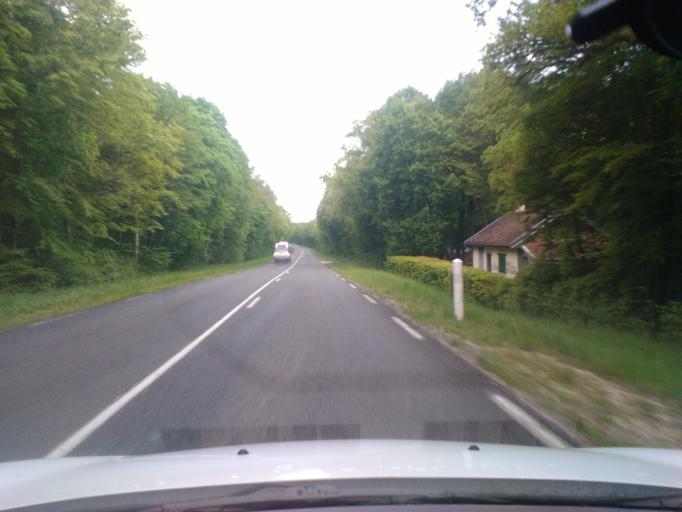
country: FR
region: Champagne-Ardenne
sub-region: Departement de la Haute-Marne
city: Lavilleneuve-au-Roi
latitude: 48.2090
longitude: 4.9301
